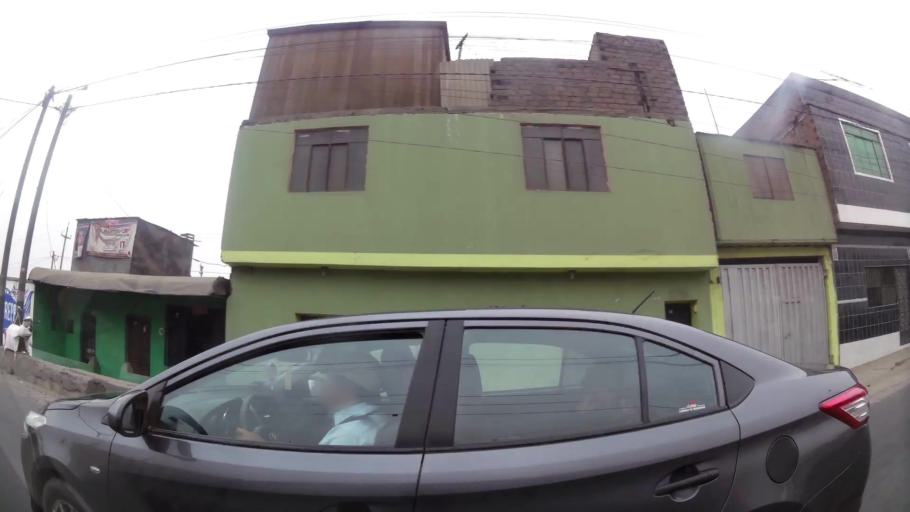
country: PE
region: Lima
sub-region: Lima
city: Santa Maria
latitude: -12.0202
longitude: -76.9024
